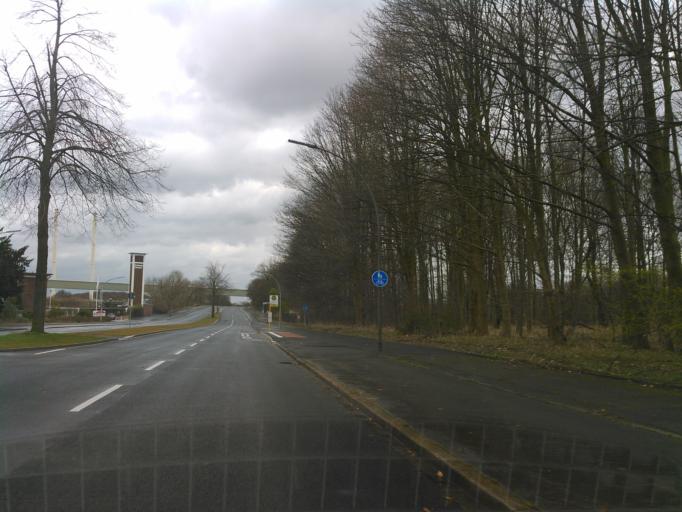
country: DE
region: North Rhine-Westphalia
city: Marl
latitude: 51.5960
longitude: 7.0654
